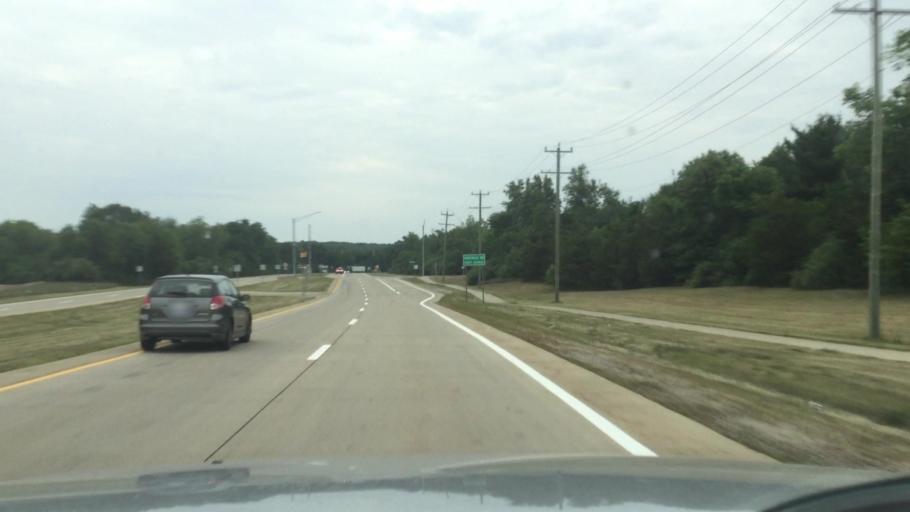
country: US
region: Michigan
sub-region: Oakland County
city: Waterford
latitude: 42.6675
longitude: -83.4385
